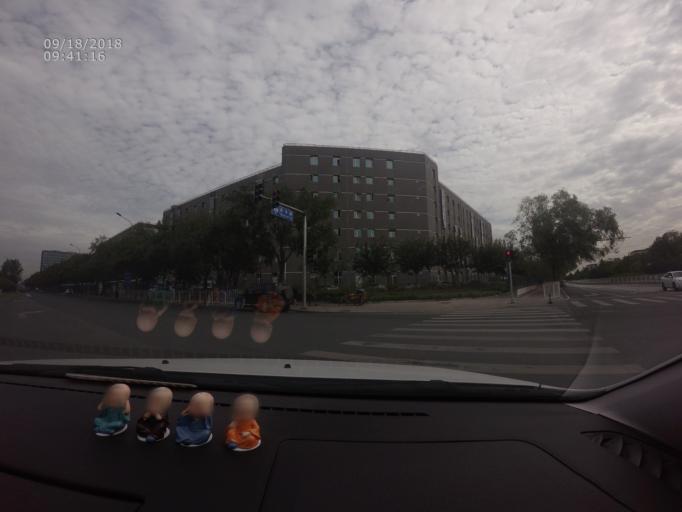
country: CN
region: Beijing
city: Xibeiwang
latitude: 40.0667
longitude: 116.2412
